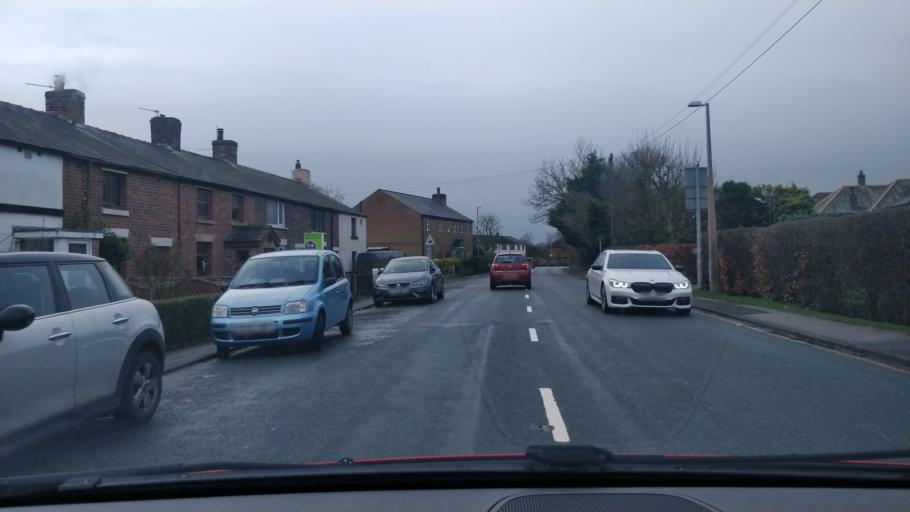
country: GB
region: England
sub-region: Lancashire
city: Preston
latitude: 53.7327
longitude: -2.7660
